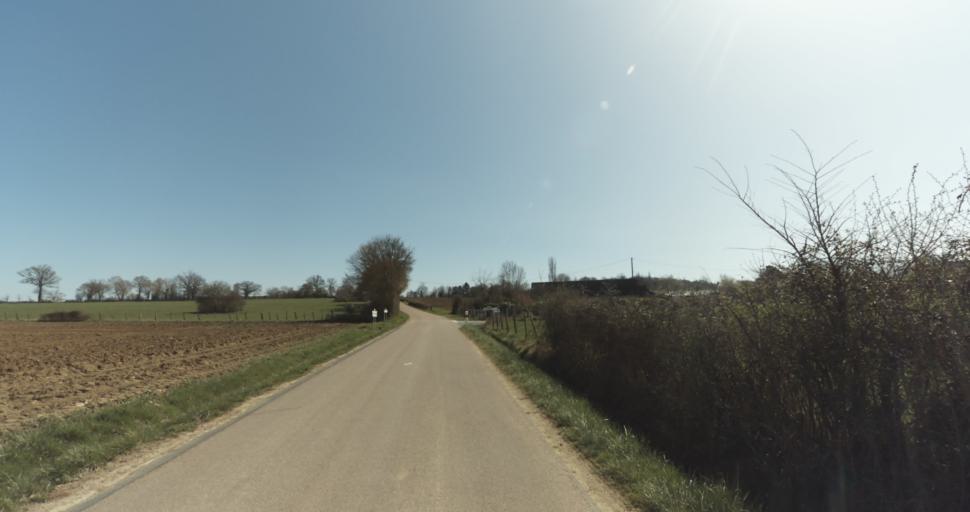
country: FR
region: Lower Normandy
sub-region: Departement du Calvados
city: Saint-Pierre-sur-Dives
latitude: 48.9643
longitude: -0.0026
